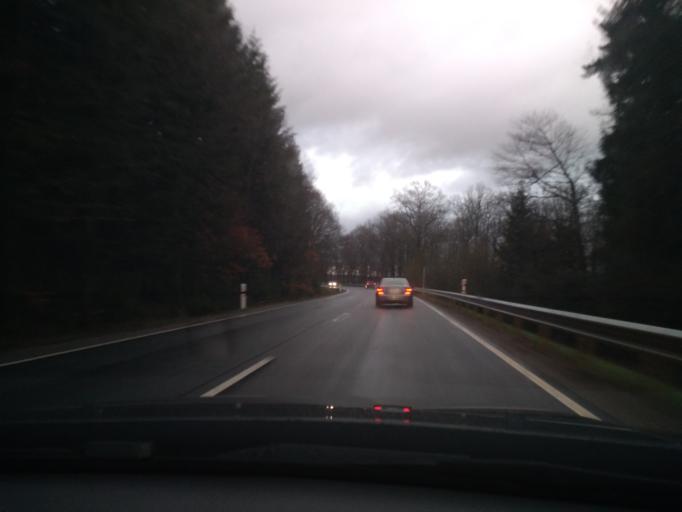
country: DE
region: Rheinland-Pfalz
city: Thalfang
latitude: 49.7602
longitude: 6.9758
